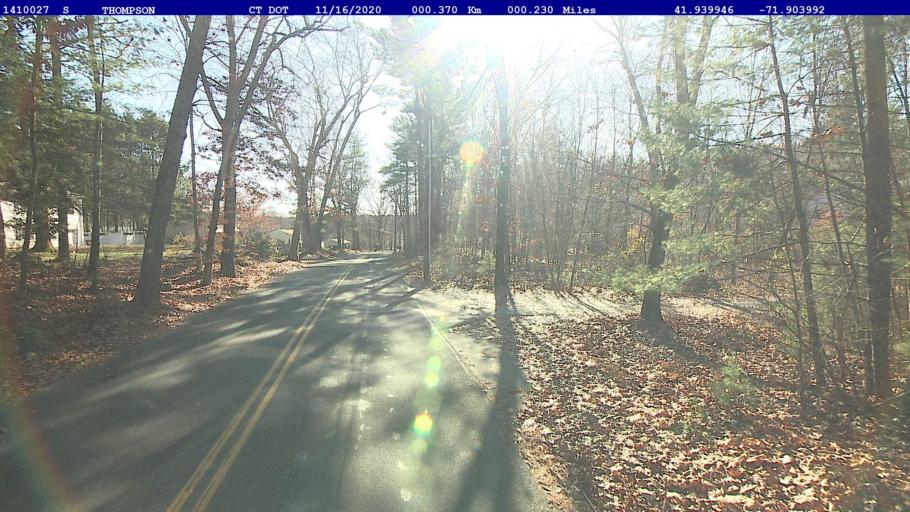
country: US
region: Connecticut
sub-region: Windham County
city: Putnam
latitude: 41.9399
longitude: -71.9040
